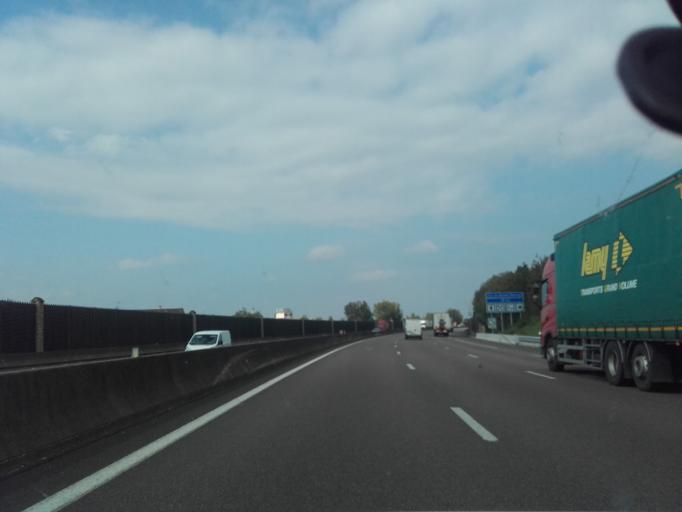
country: FR
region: Bourgogne
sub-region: Departement de Saone-et-Loire
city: Saint-Remy
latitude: 46.7718
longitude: 4.8202
